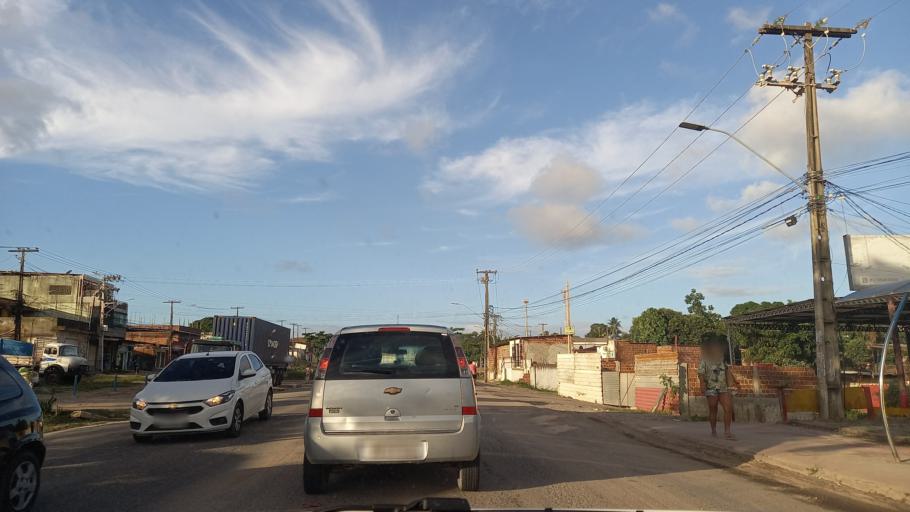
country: BR
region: Pernambuco
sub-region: Jaboatao Dos Guararapes
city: Jaboatao
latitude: -8.2409
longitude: -34.9870
